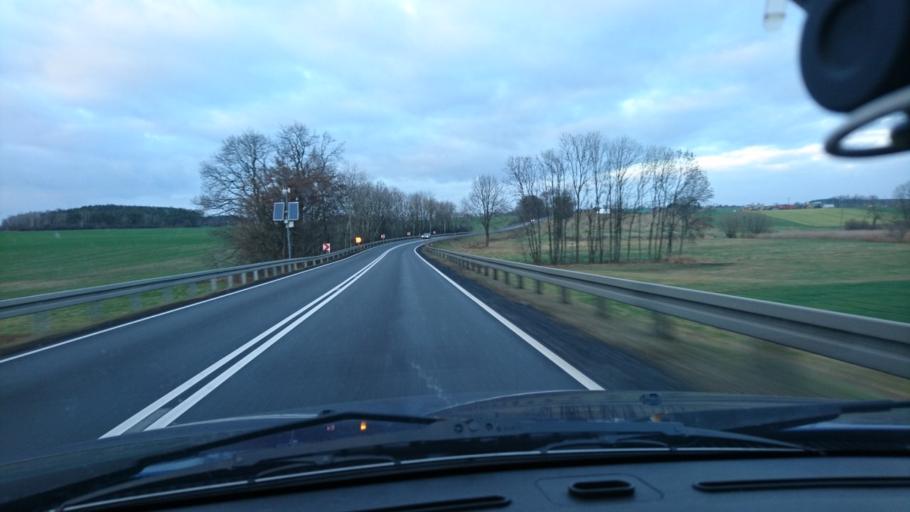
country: PL
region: Greater Poland Voivodeship
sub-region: Powiat ostrzeszowski
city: Ostrzeszow
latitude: 51.3746
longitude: 17.9427
